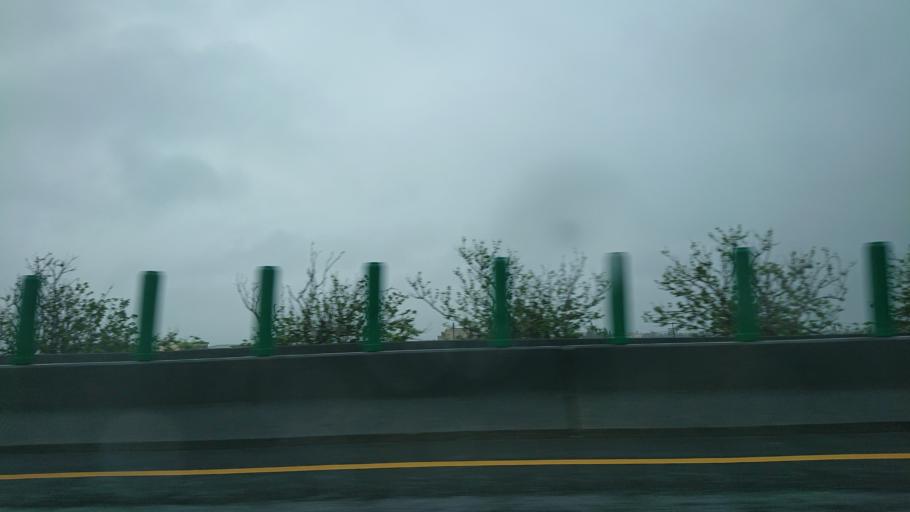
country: TW
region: Taiwan
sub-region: Chiayi
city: Taibao
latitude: 23.7127
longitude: 120.2002
